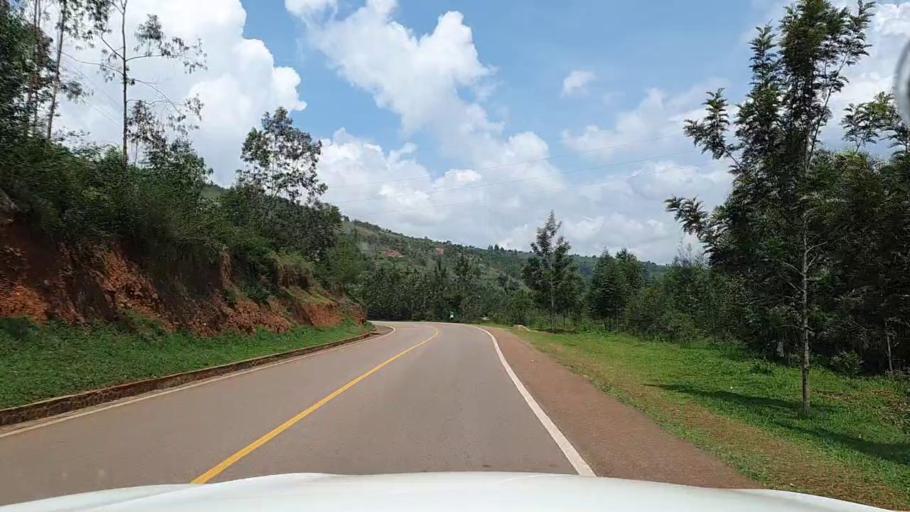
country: RW
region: Kigali
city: Kigali
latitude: -1.8370
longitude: 30.0813
